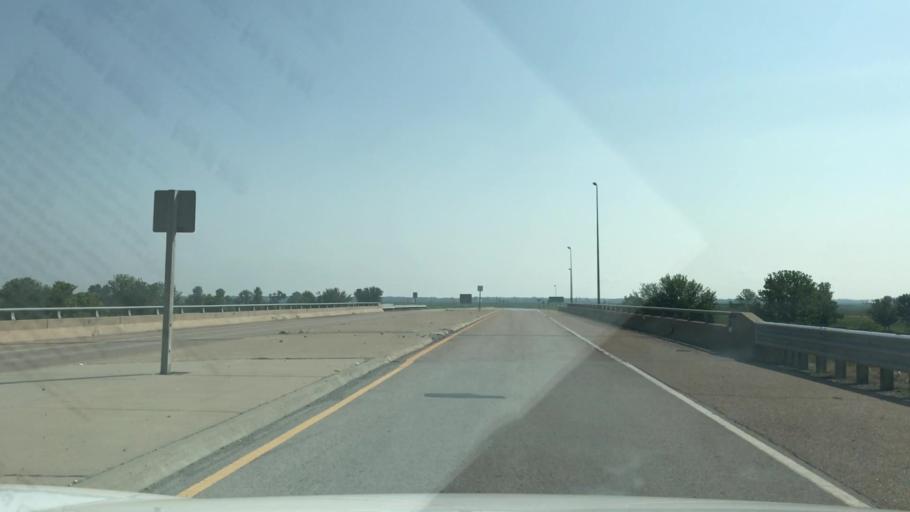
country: US
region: Illinois
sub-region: Washington County
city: Okawville
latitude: 38.4395
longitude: -89.5307
